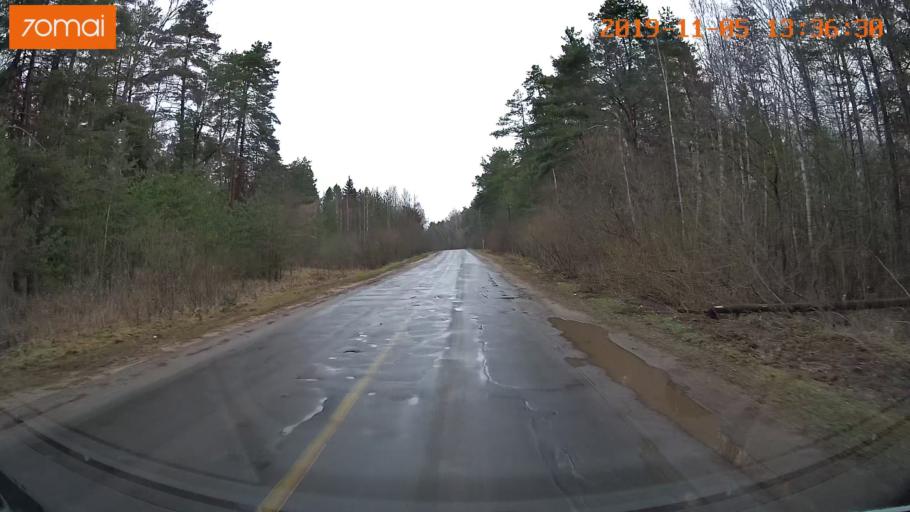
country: RU
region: Ivanovo
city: Shuya
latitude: 56.9150
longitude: 41.3823
